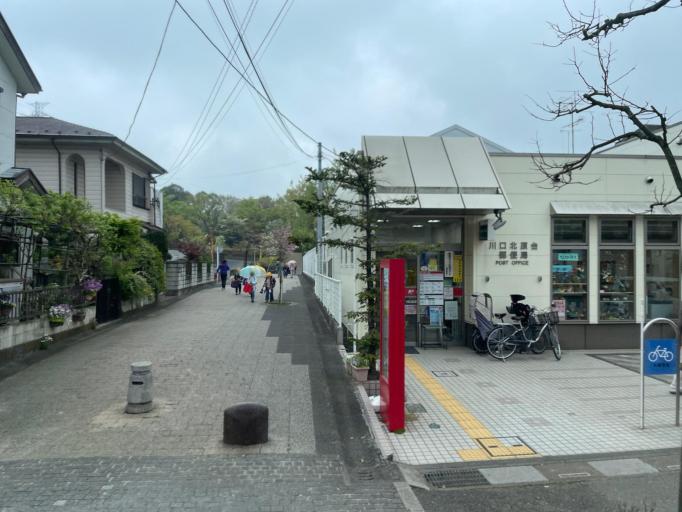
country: JP
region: Saitama
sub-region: Kawaguchi-shi
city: Hatogaya-honcho
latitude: 35.8698
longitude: 139.7302
